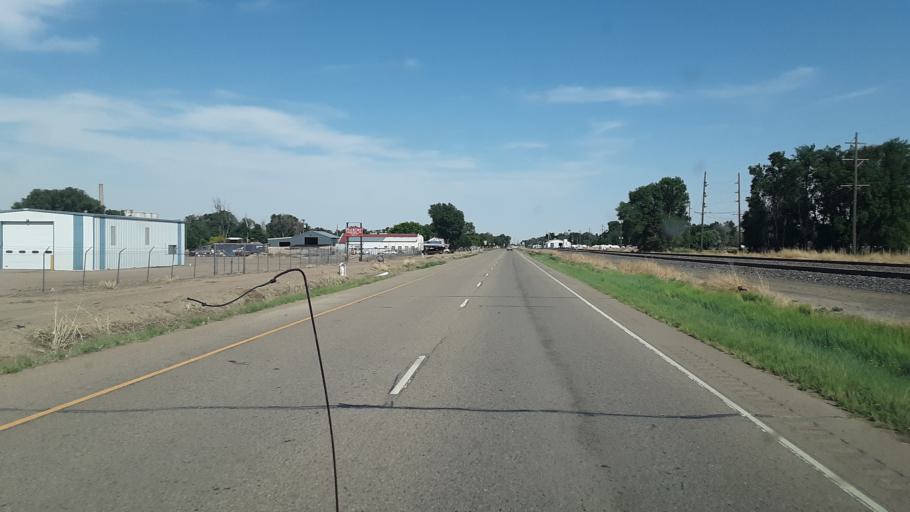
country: US
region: Colorado
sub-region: Otero County
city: Rocky Ford
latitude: 38.0597
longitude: -103.7365
